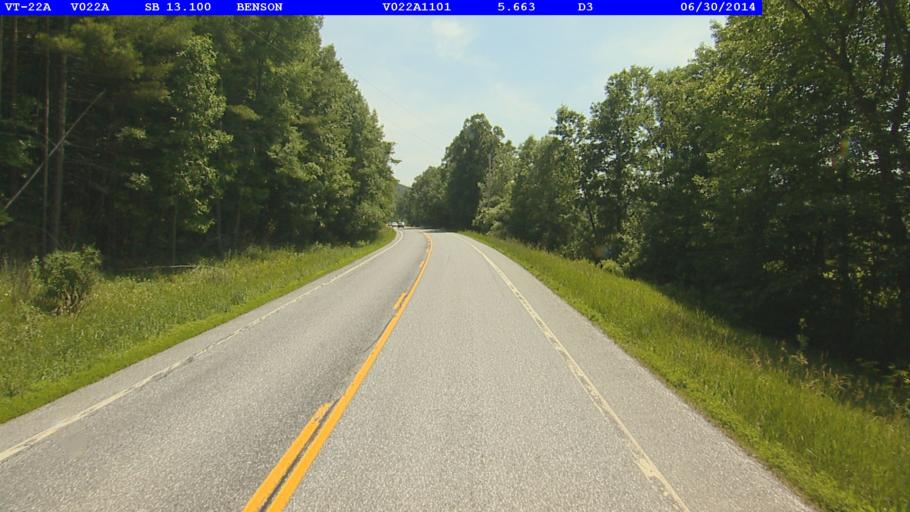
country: US
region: New York
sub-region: Essex County
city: Ticonderoga
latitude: 43.7490
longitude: -73.3083
